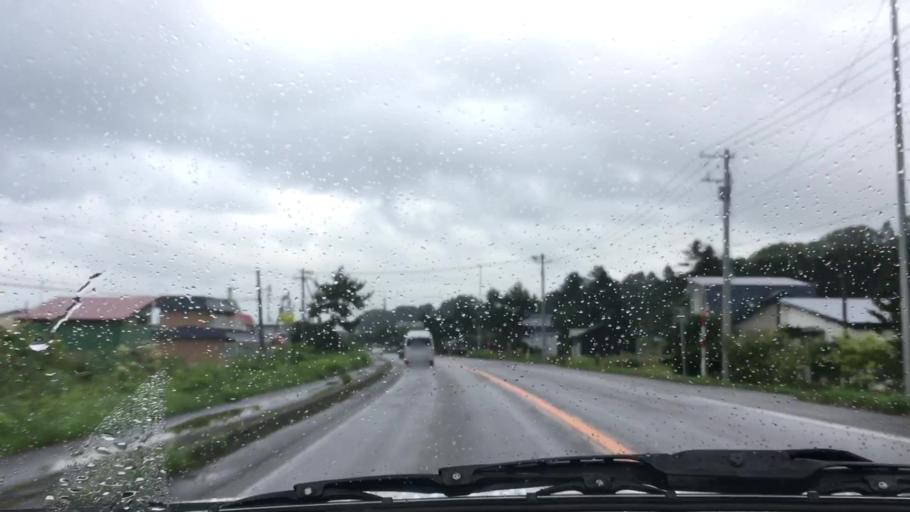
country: JP
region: Hokkaido
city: Nanae
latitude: 42.2243
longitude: 140.3468
